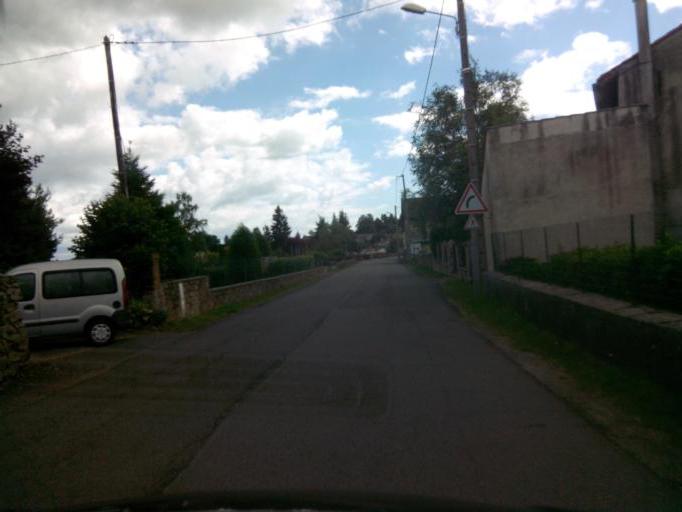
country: FR
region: Rhone-Alpes
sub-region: Departement de la Loire
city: Usson-en-Forez
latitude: 45.3827
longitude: 3.9975
